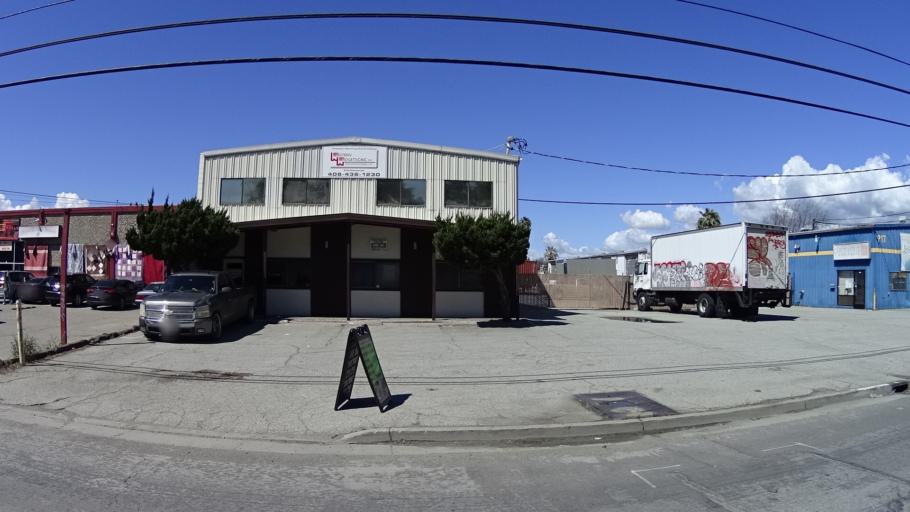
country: US
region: California
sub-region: Santa Clara County
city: San Jose
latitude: 37.3672
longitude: -121.8880
